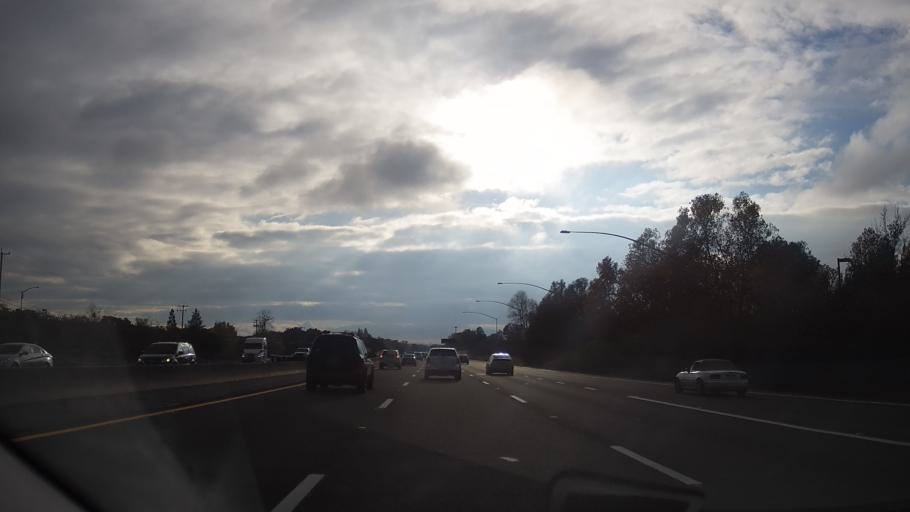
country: US
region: California
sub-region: Placer County
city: Rocklin
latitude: 38.7867
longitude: -121.2250
